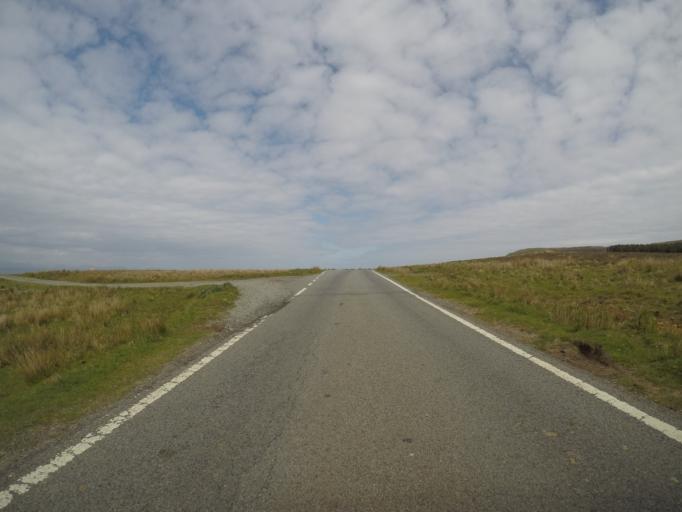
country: GB
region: Scotland
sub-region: Highland
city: Portree
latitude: 57.6588
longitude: -6.3734
